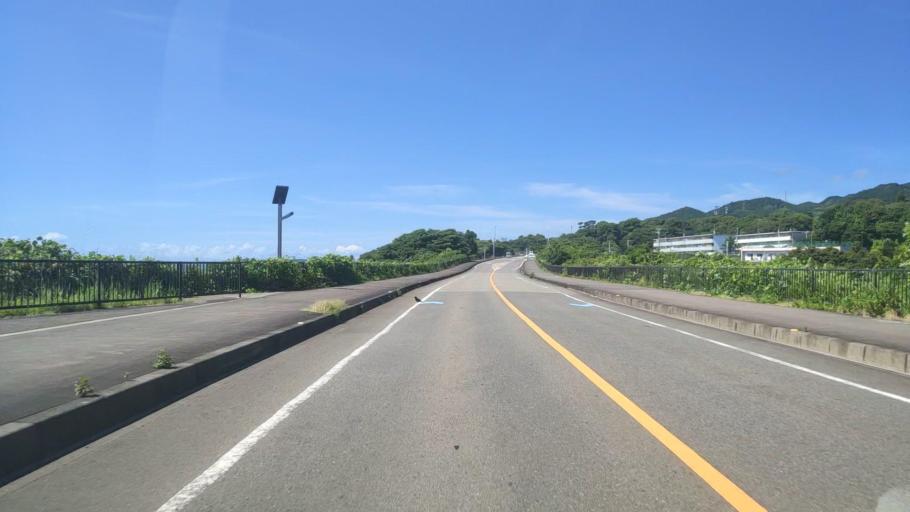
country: JP
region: Wakayama
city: Shingu
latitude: 33.7130
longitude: 135.9997
